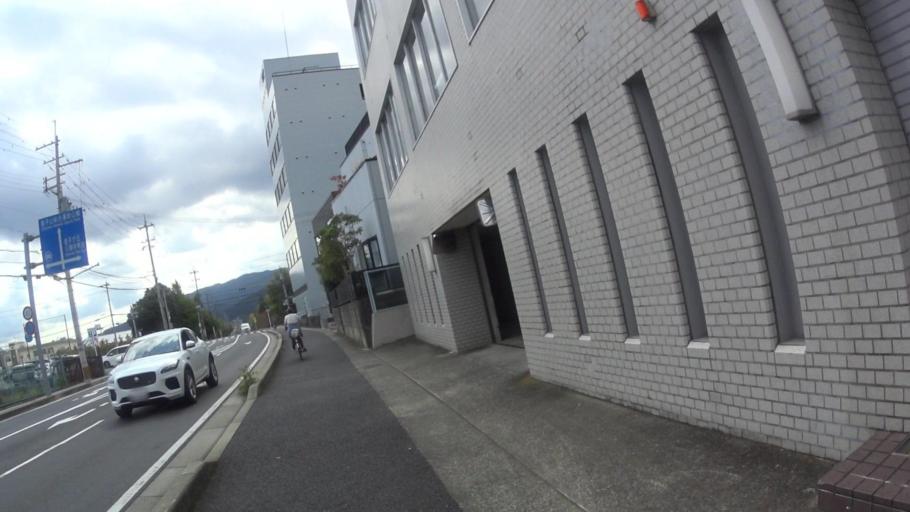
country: JP
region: Shiga Prefecture
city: Otsu-shi
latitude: 35.0224
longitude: 135.8580
